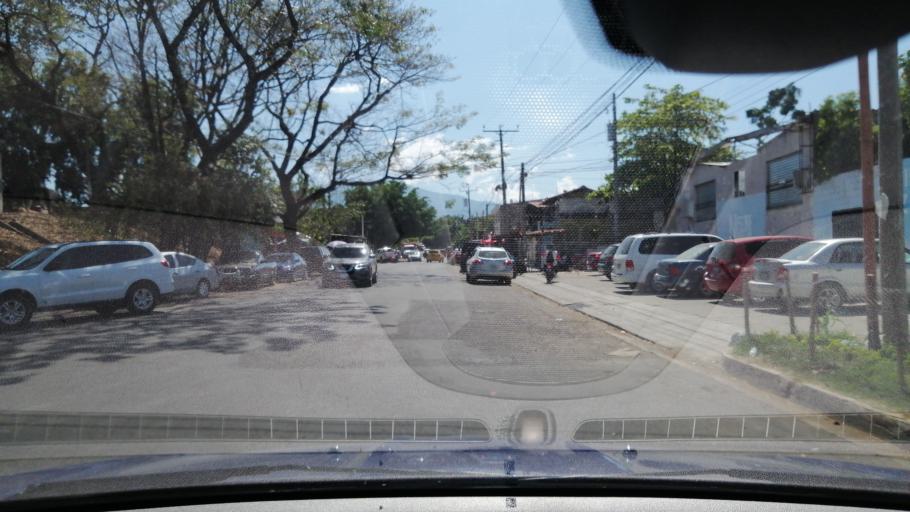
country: SV
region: Santa Ana
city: Santa Ana
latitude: 13.9634
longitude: -89.5705
